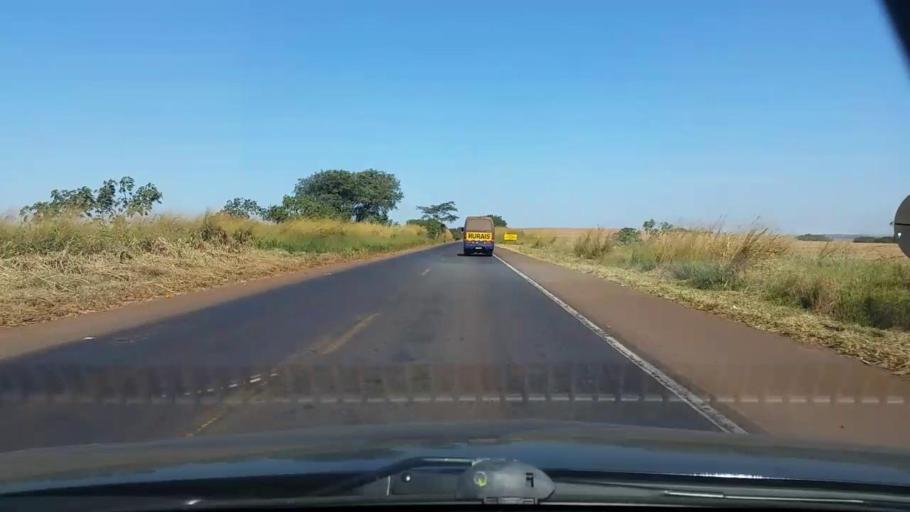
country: BR
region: Sao Paulo
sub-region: Igaracu Do Tiete
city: Igaracu do Tiete
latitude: -22.5670
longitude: -48.5638
